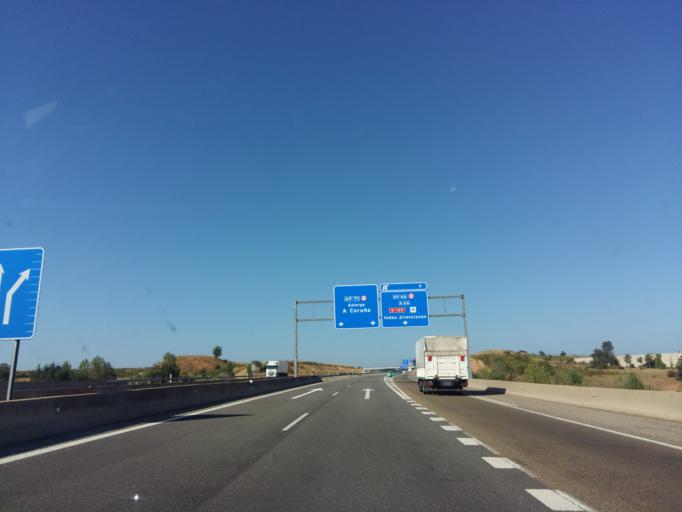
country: ES
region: Castille and Leon
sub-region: Provincia de Leon
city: San Andres del Rabanedo
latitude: 42.5716
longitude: -5.6385
